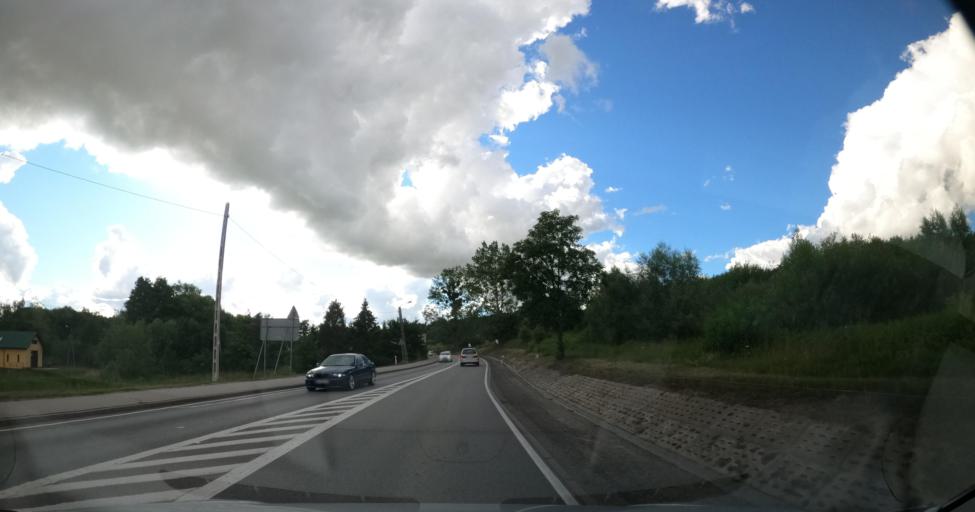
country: PL
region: Pomeranian Voivodeship
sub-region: Powiat kartuski
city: Zukowo
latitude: 54.3372
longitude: 18.4036
